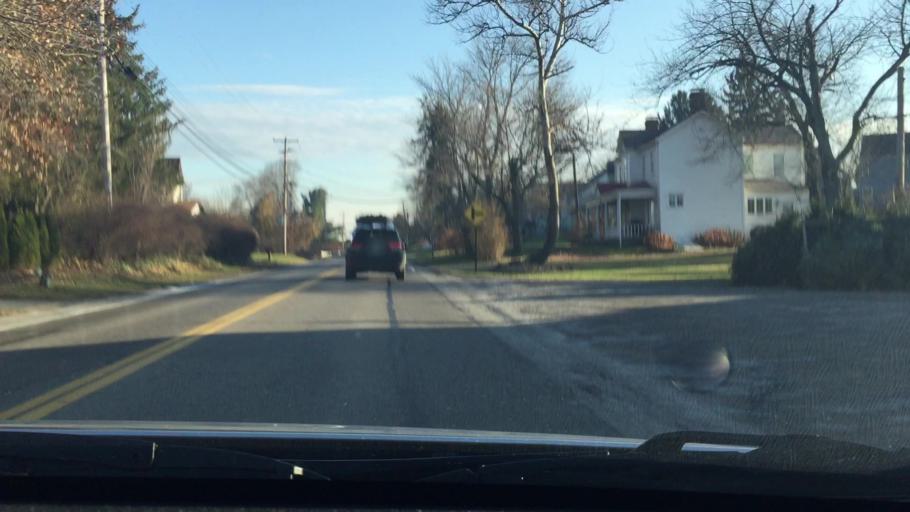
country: US
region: Pennsylvania
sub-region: Allegheny County
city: Franklin Park
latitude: 40.6071
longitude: -80.0883
